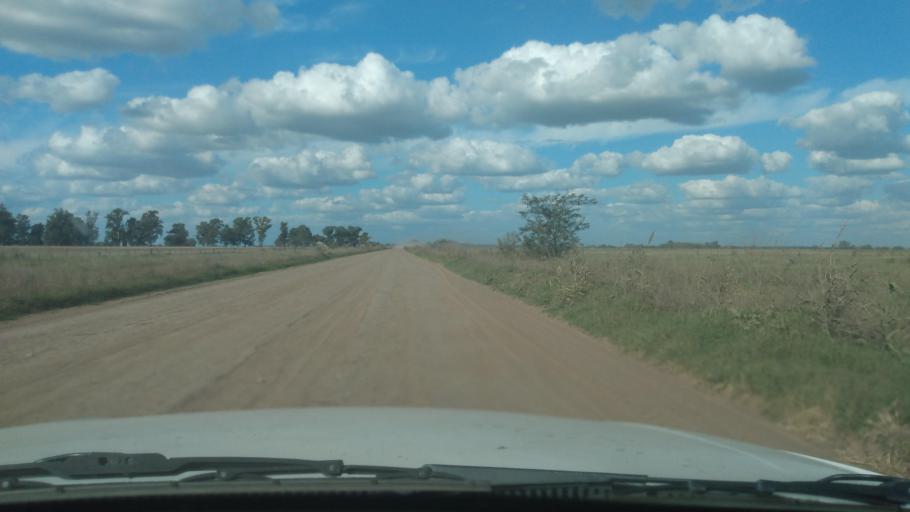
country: AR
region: Buenos Aires
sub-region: Partido de Navarro
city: Navarro
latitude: -35.0123
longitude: -59.4466
